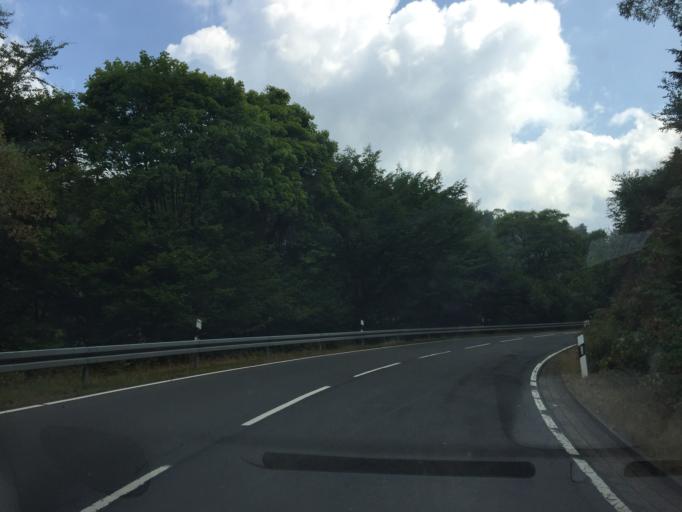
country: DE
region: Lower Saxony
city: Zorge
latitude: 51.6492
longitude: 10.6437
